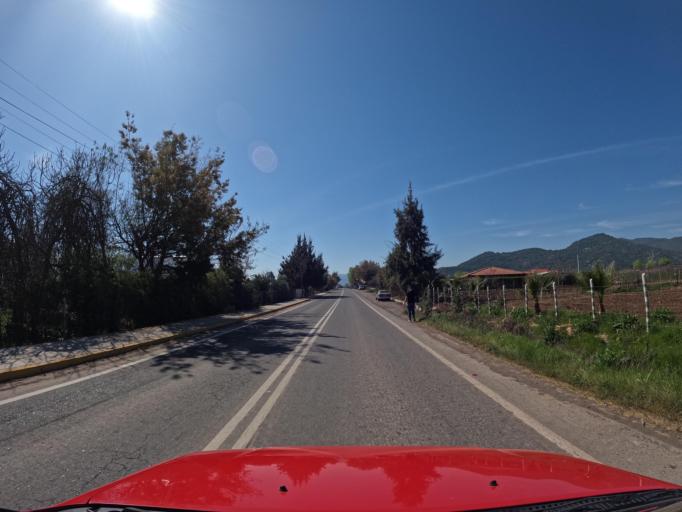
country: CL
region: Maule
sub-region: Provincia de Curico
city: Rauco
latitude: -35.0518
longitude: -71.4761
